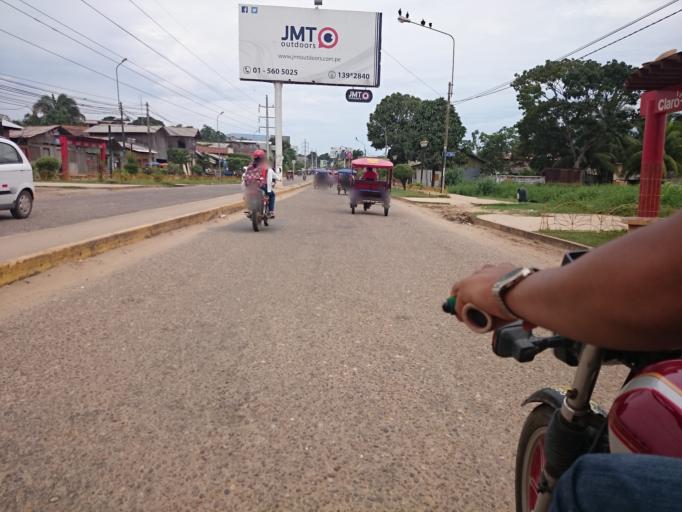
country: PE
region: Ucayali
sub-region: Provincia de Coronel Portillo
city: Pucallpa
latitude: -8.3679
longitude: -74.5626
